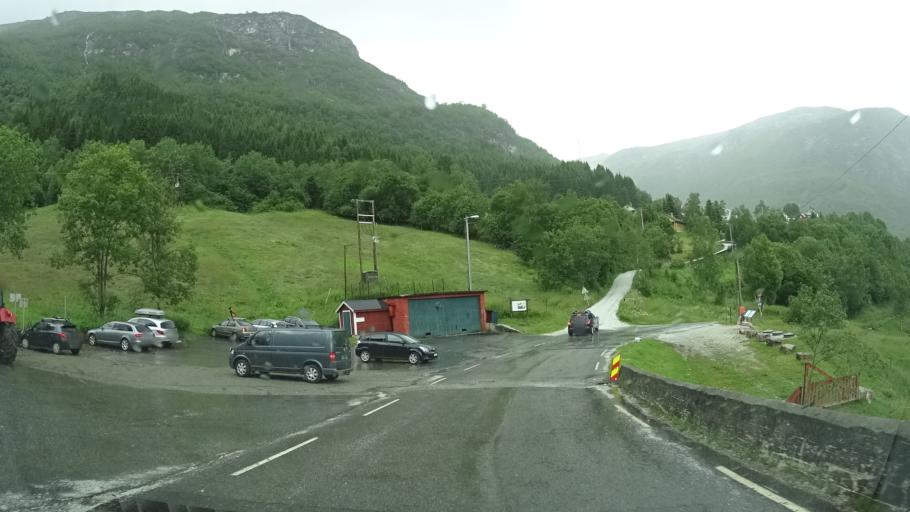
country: NO
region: Sogn og Fjordane
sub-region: Vik
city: Vik
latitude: 60.8359
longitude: 6.6800
